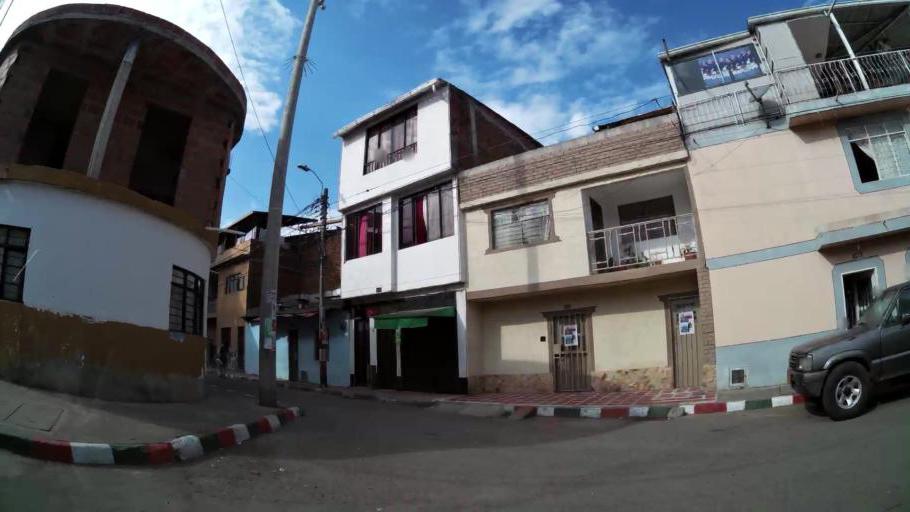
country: CO
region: Valle del Cauca
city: Cali
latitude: 3.4647
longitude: -76.5174
